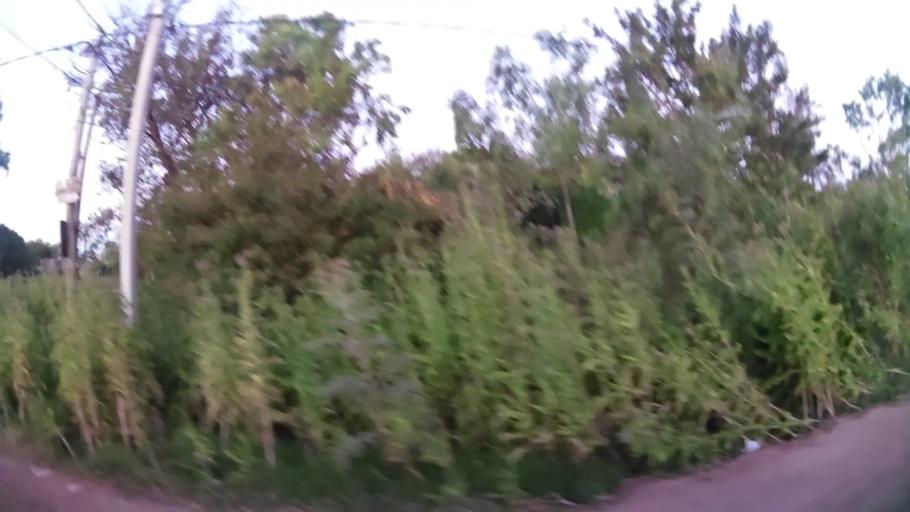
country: UY
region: Canelones
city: Colonia Nicolich
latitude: -34.8118
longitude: -55.9623
